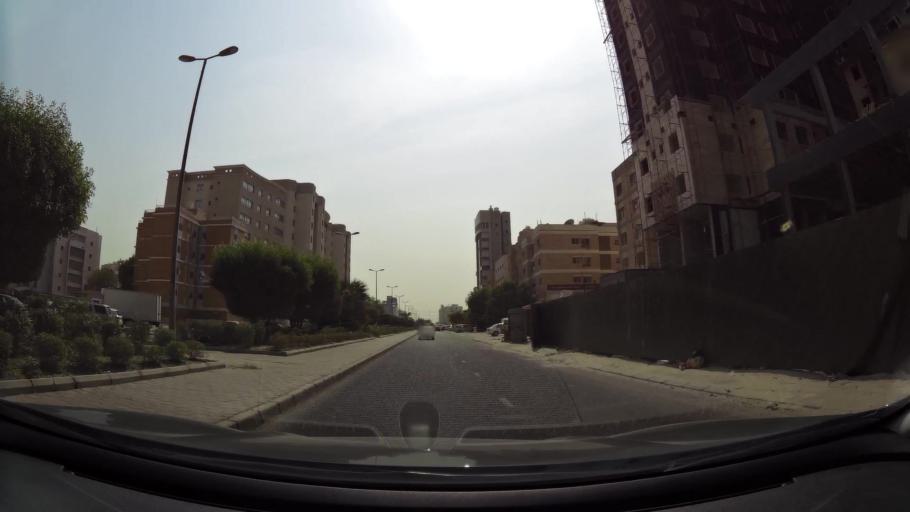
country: KW
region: Al Asimah
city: Ar Rabiyah
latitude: 29.3079
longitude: 47.9147
